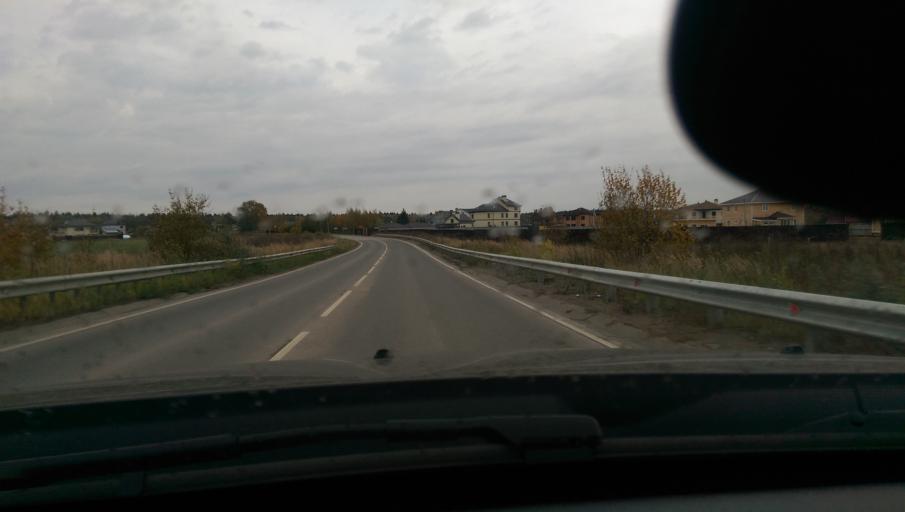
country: RU
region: Moskovskaya
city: Pirogovskiy
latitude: 56.0080
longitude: 37.7223
